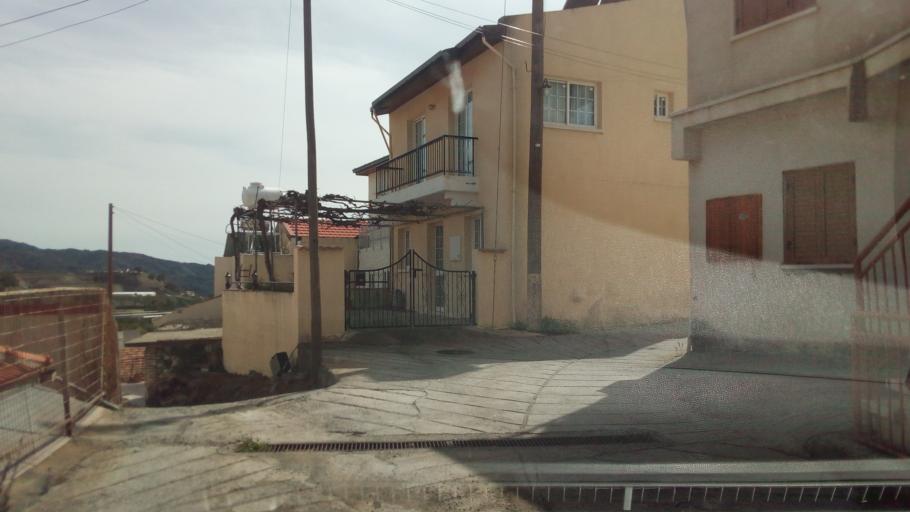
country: CY
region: Limassol
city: Pelendri
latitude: 34.8946
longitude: 32.9643
